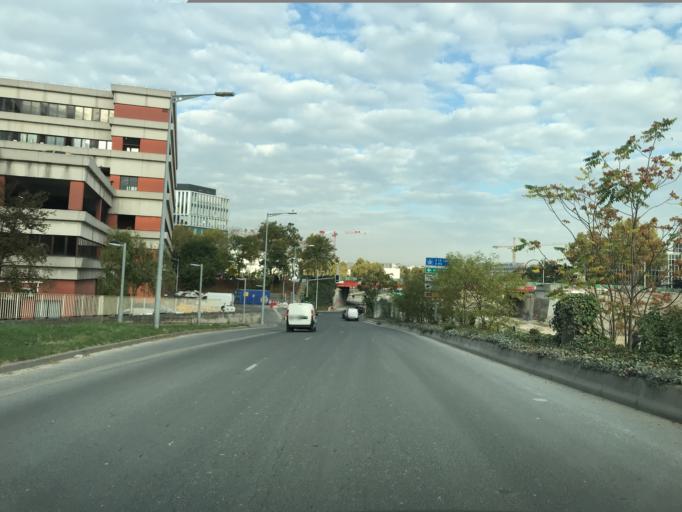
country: FR
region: Ile-de-France
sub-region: Departement des Hauts-de-Seine
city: Nanterre
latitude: 48.8979
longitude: 2.2225
